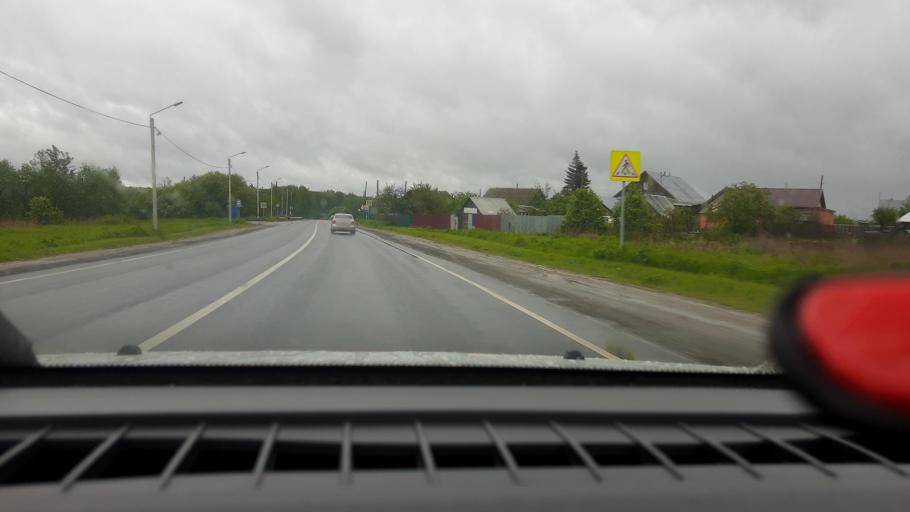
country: RU
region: Nizjnij Novgorod
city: Linda
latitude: 56.6002
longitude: 44.0428
